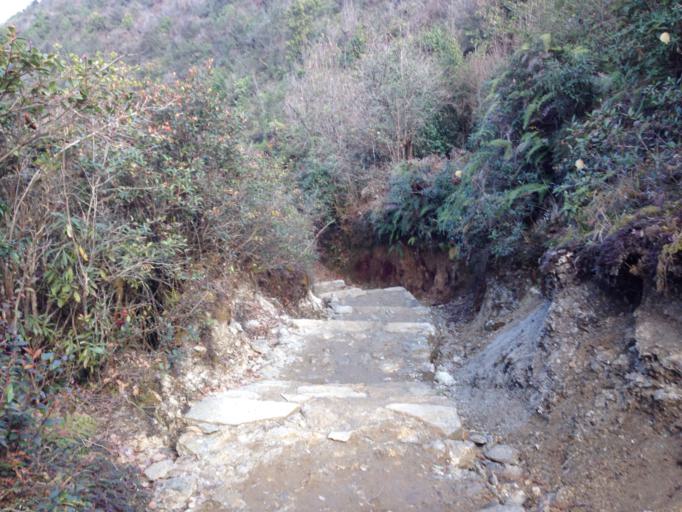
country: NP
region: Central Region
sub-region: Bagmati Zone
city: Nagarkot
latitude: 27.8154
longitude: 85.4470
